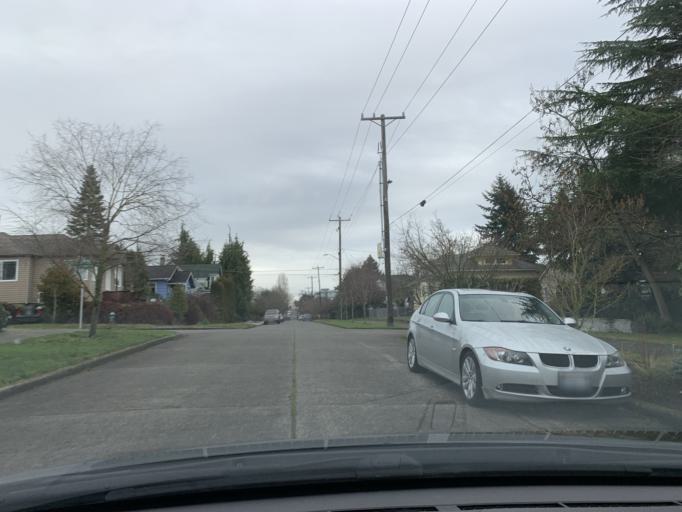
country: US
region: Washington
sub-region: King County
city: White Center
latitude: 47.5522
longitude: -122.3915
